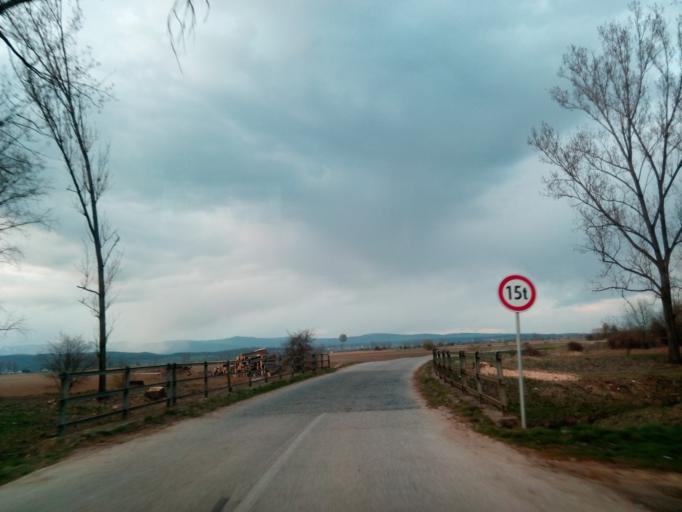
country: SK
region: Kosicky
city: Moldava nad Bodvou
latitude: 48.5619
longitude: 20.9601
